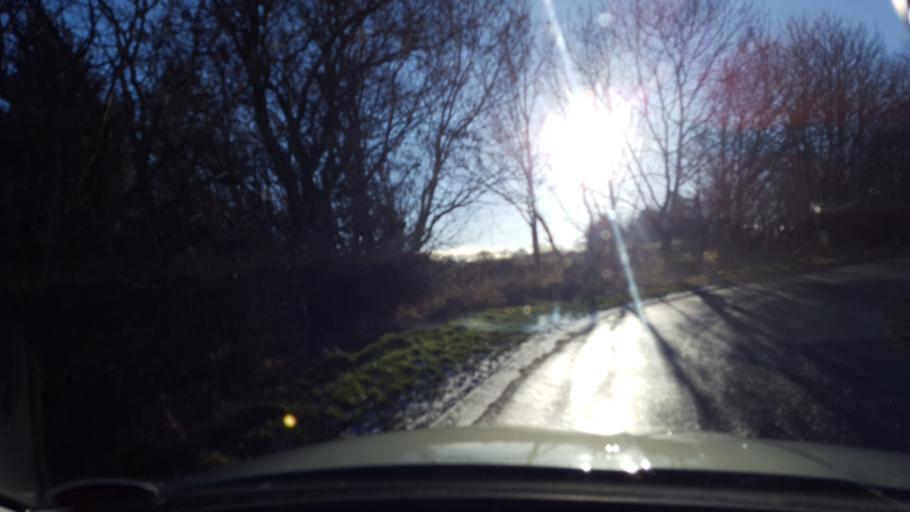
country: GB
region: Scotland
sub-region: West Lothian
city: Livingston
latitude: 55.9596
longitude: -3.5341
